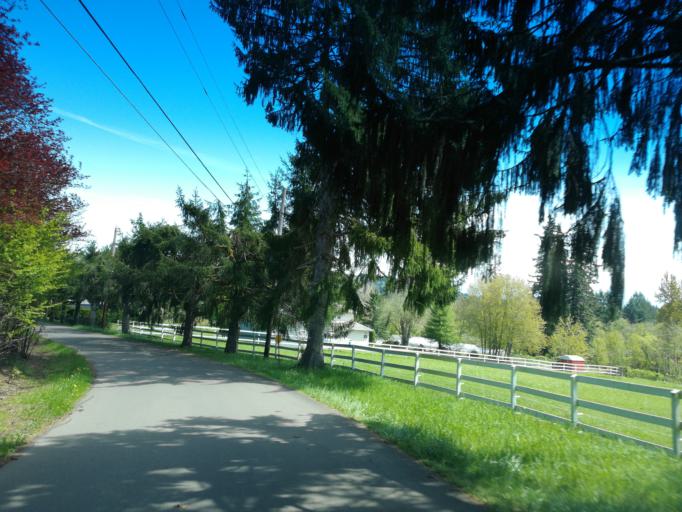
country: US
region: Oregon
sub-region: Multnomah County
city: Gresham
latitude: 45.4514
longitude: -122.4227
